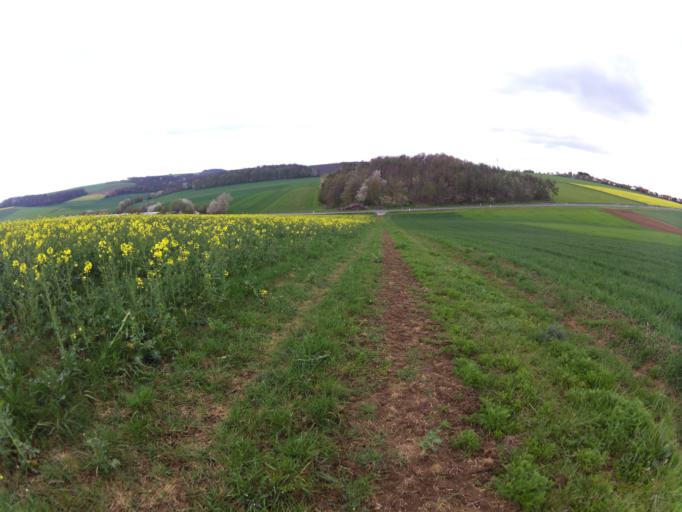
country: DE
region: Bavaria
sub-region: Regierungsbezirk Unterfranken
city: Hettstadt
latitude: 49.7978
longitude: 9.8012
